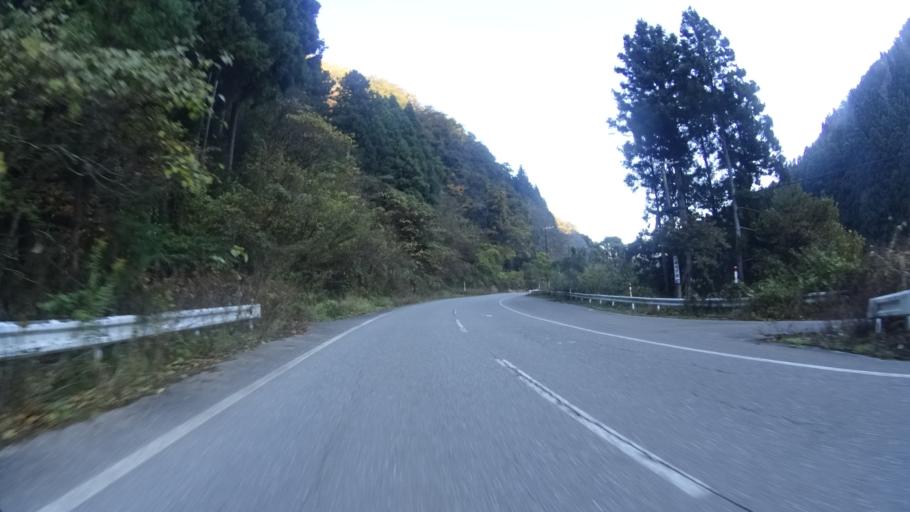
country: JP
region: Fukui
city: Maruoka
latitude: 36.2008
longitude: 136.3450
